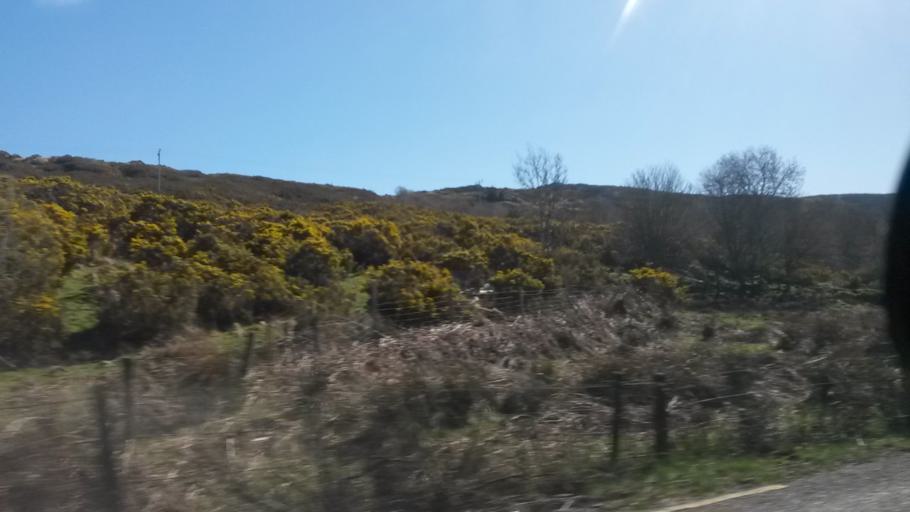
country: IE
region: Munster
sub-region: Ciarrai
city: Cill Airne
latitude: 51.9447
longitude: -9.3865
